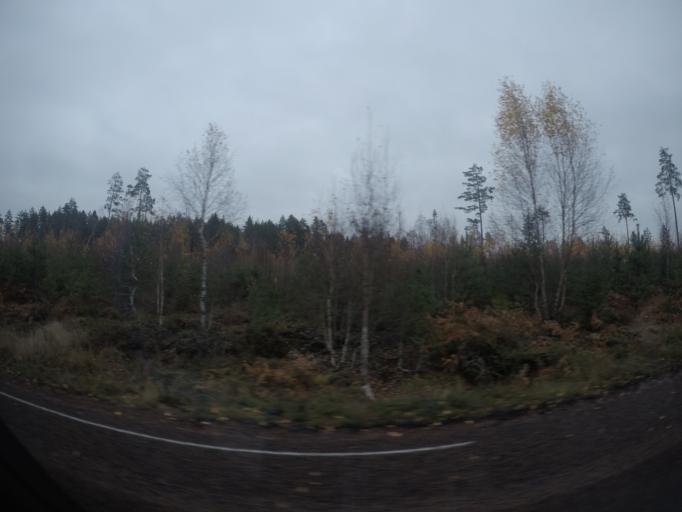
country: SE
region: Vaestmanland
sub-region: Surahammars Kommun
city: Surahammar
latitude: 59.6646
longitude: 16.0827
